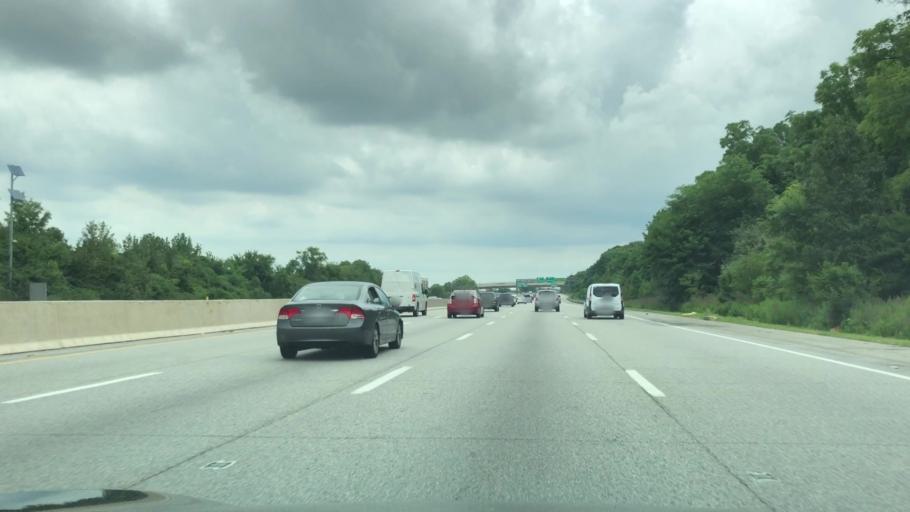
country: US
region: Pennsylvania
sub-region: Montgomery County
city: King of Prussia
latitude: 40.0753
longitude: -75.4190
